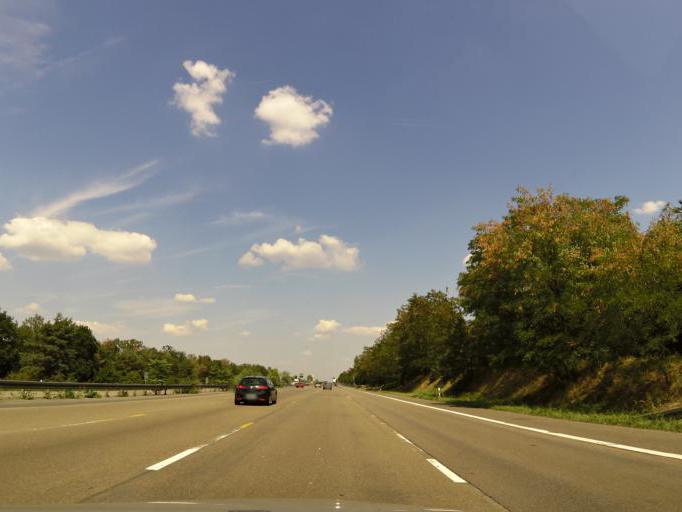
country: DE
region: Hesse
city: Weiterstadt
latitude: 49.8773
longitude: 8.6022
